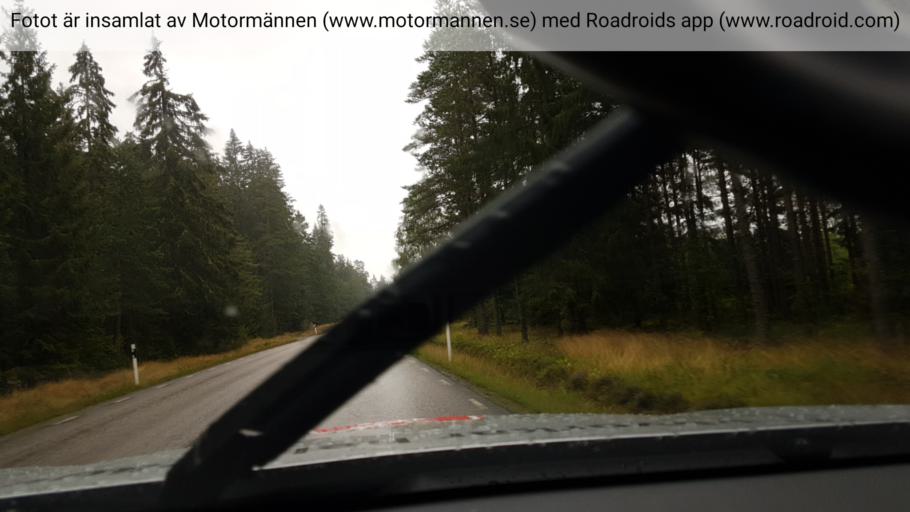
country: SE
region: Vaestra Goetaland
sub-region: Bengtsfors Kommun
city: Dals Langed
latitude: 58.8354
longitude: 12.1472
